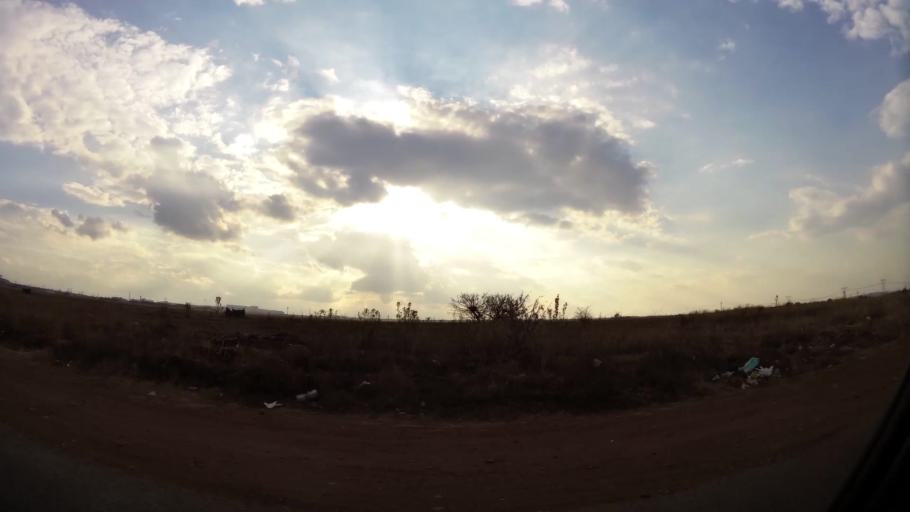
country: ZA
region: Gauteng
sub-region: Sedibeng District Municipality
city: Vereeniging
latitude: -26.6531
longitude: 27.8733
